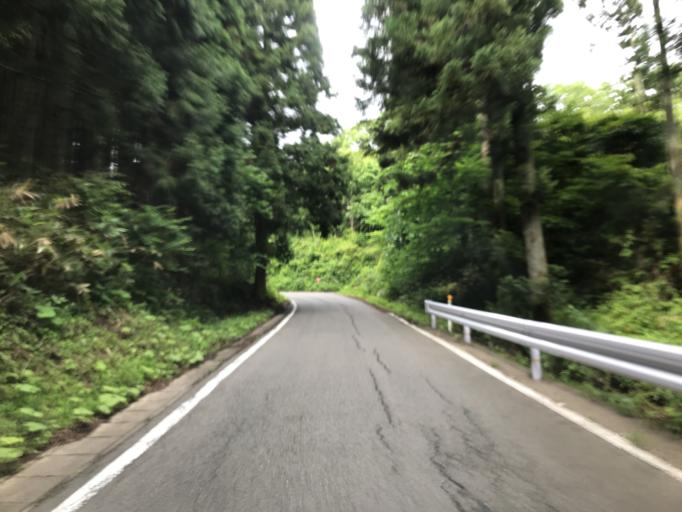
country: JP
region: Fukushima
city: Funehikimachi-funehiki
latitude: 37.4678
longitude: 140.6401
